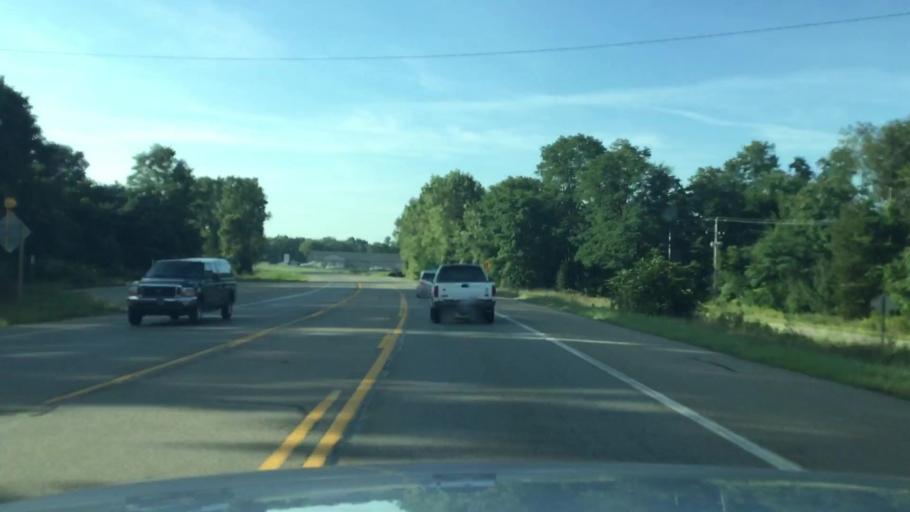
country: US
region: Michigan
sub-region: Jackson County
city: Vandercook Lake
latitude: 42.1887
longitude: -84.3696
